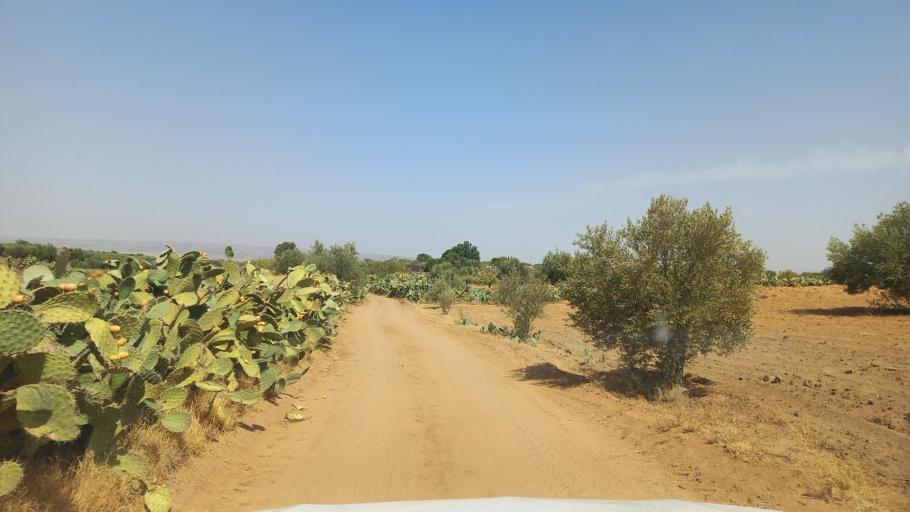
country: TN
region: Al Qasrayn
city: Kasserine
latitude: 35.2481
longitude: 9.0529
